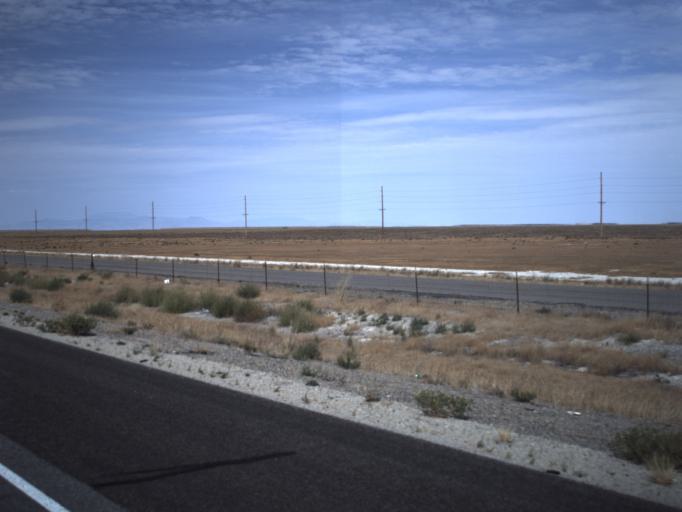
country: US
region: Utah
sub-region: Tooele County
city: Grantsville
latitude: 40.7262
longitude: -113.1649
